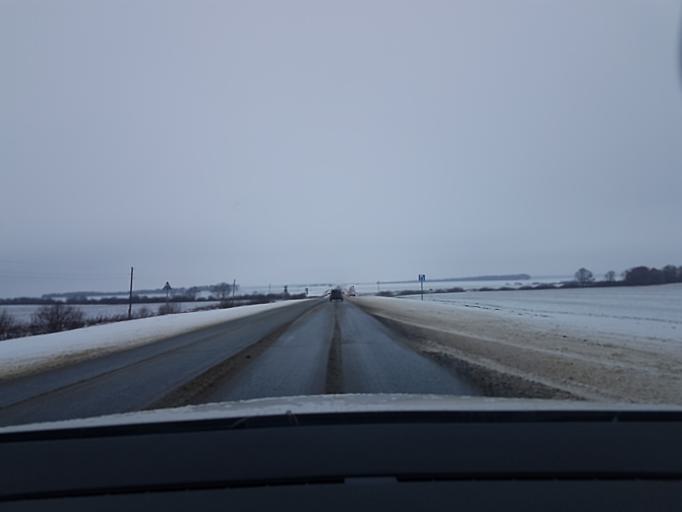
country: RU
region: Moskovskaya
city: Serebryanyye Prudy
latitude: 54.3789
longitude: 38.7313
